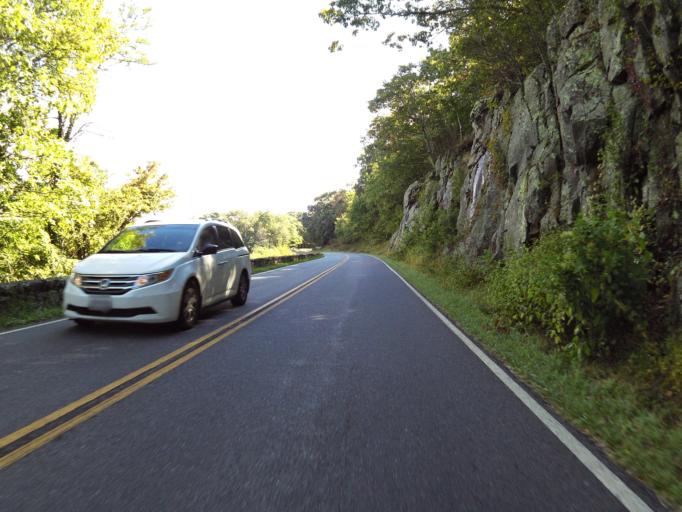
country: US
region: Virginia
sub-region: Page County
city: Stanley
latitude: 38.5239
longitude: -78.4281
